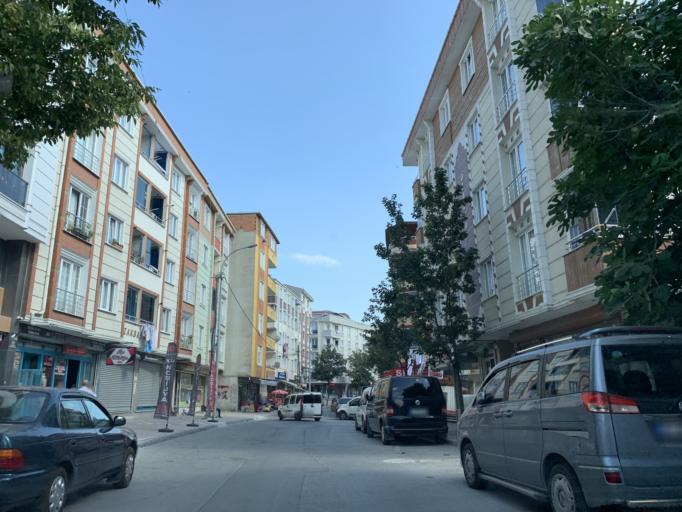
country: TR
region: Istanbul
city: Esenyurt
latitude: 41.0388
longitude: 28.6748
